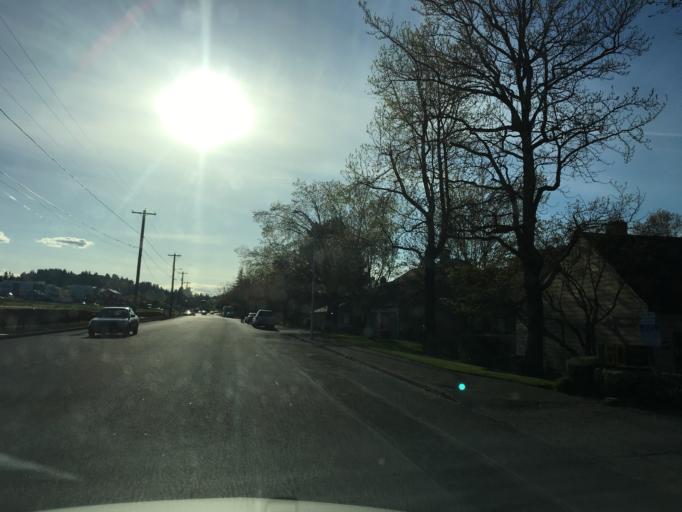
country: US
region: Oregon
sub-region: Multnomah County
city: Lents
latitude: 45.5518
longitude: -122.5327
